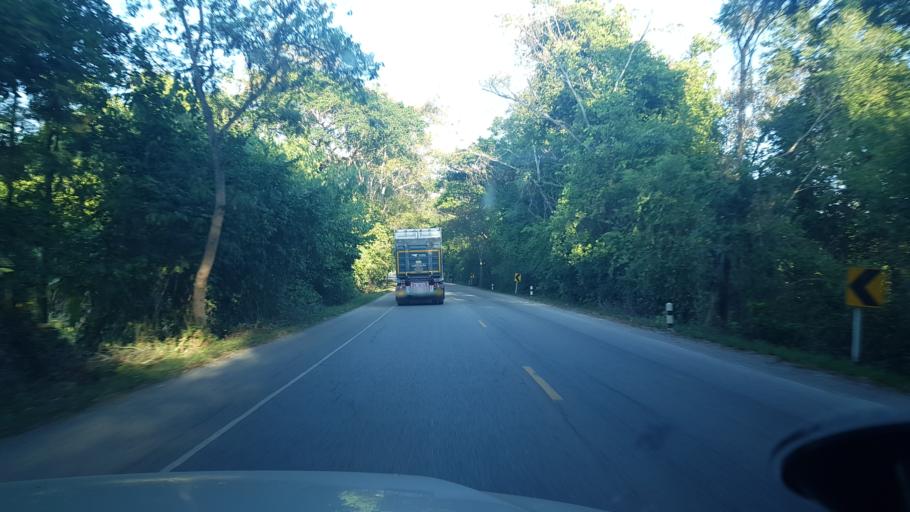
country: TH
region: Khon Kaen
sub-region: Amphoe Phu Pha Man
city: Phu Pha Man
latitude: 16.6442
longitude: 101.8211
